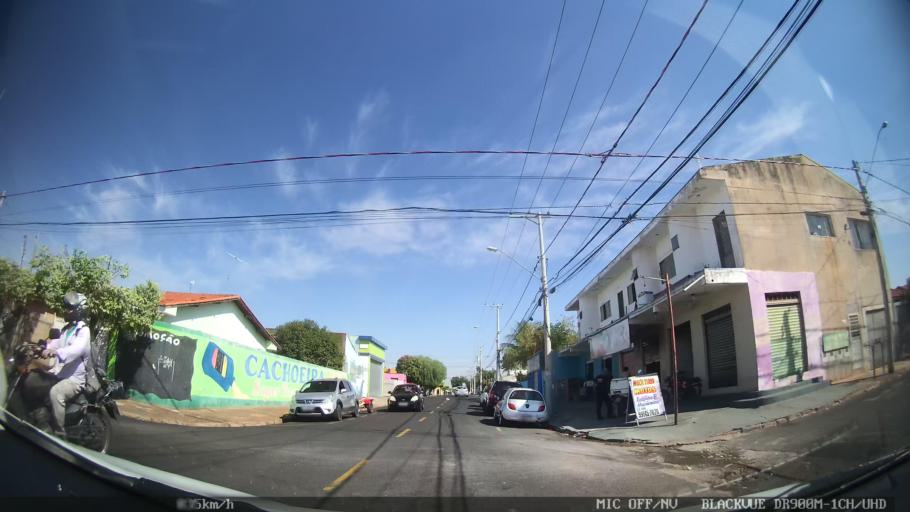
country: BR
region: Sao Paulo
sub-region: Sao Jose Do Rio Preto
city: Sao Jose do Rio Preto
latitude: -20.7792
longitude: -49.4070
